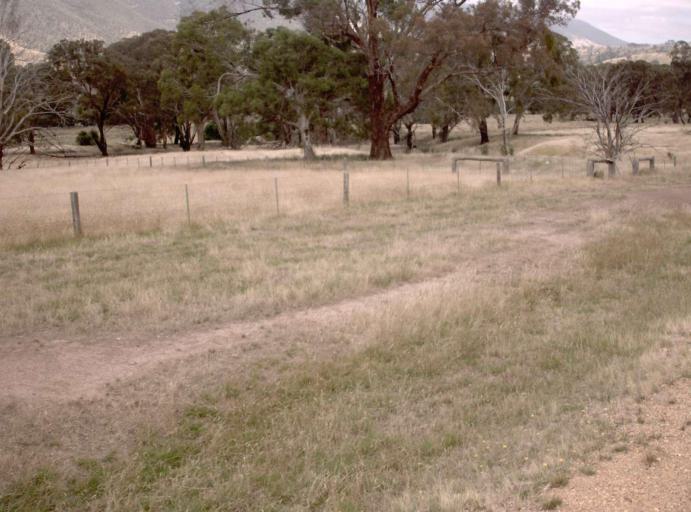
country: AU
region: Victoria
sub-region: Wellington
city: Heyfield
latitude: -37.6486
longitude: 146.6431
